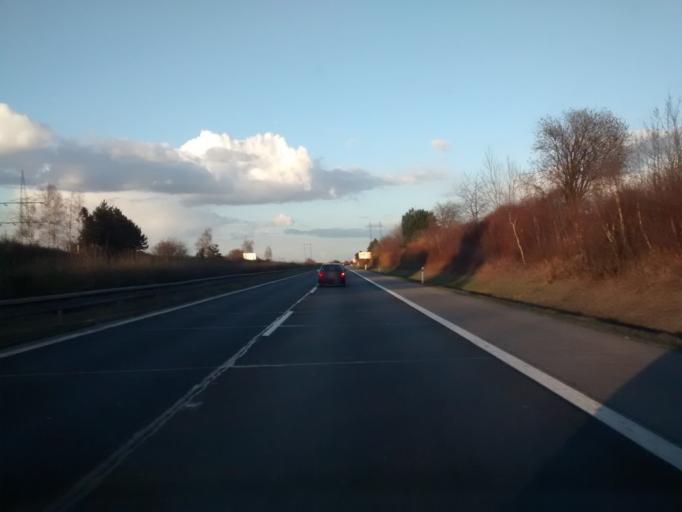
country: CZ
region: Central Bohemia
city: Zelenec
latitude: 50.1149
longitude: 14.6619
